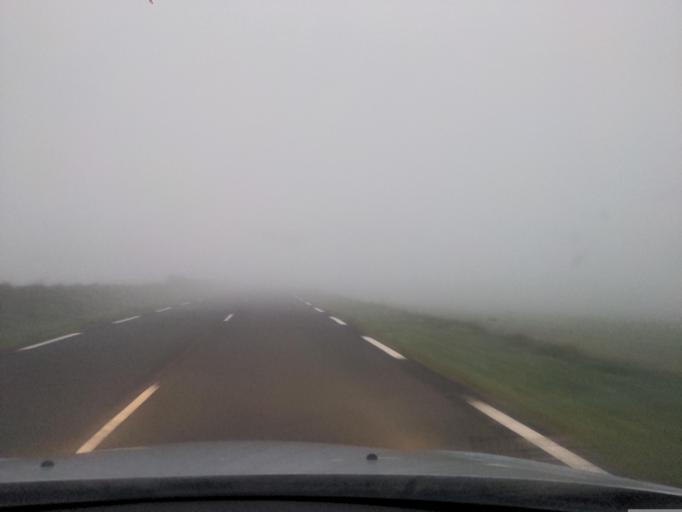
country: FR
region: Champagne-Ardenne
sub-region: Departement de la Haute-Marne
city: Langres
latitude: 47.8113
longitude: 5.2767
